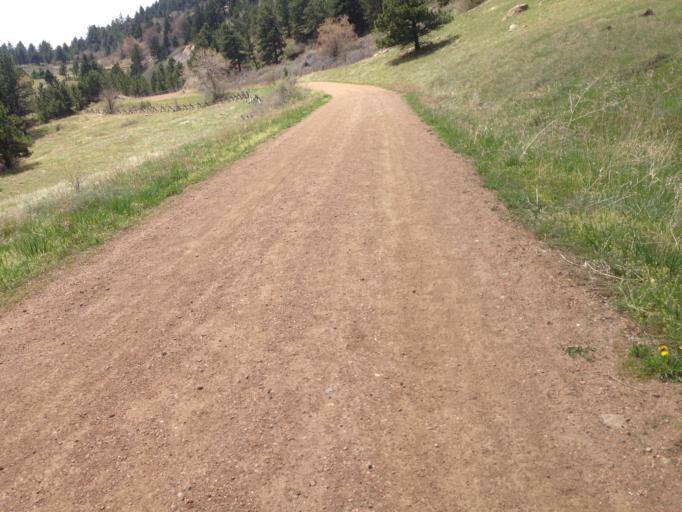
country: US
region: Colorado
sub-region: Boulder County
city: Boulder
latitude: 39.9279
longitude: -105.2725
